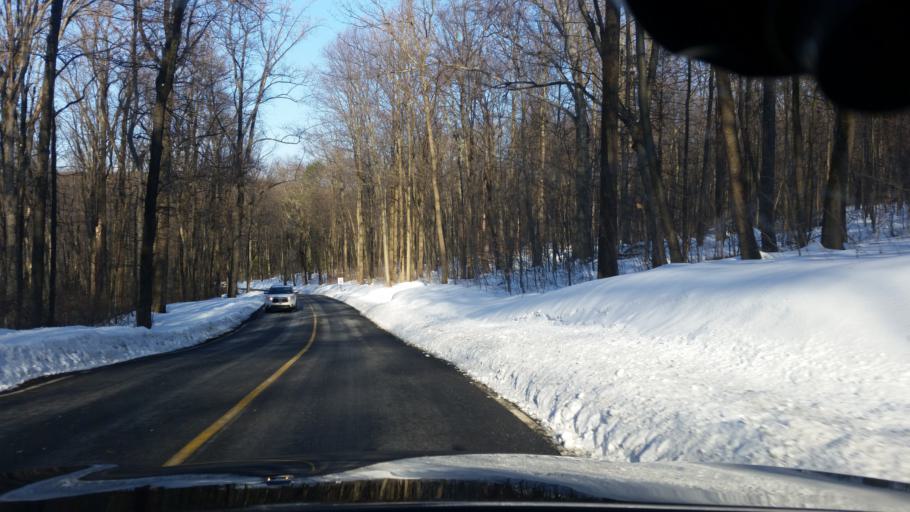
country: US
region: Pennsylvania
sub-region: Cumberland County
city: Enola
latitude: 40.3095
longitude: -77.0066
